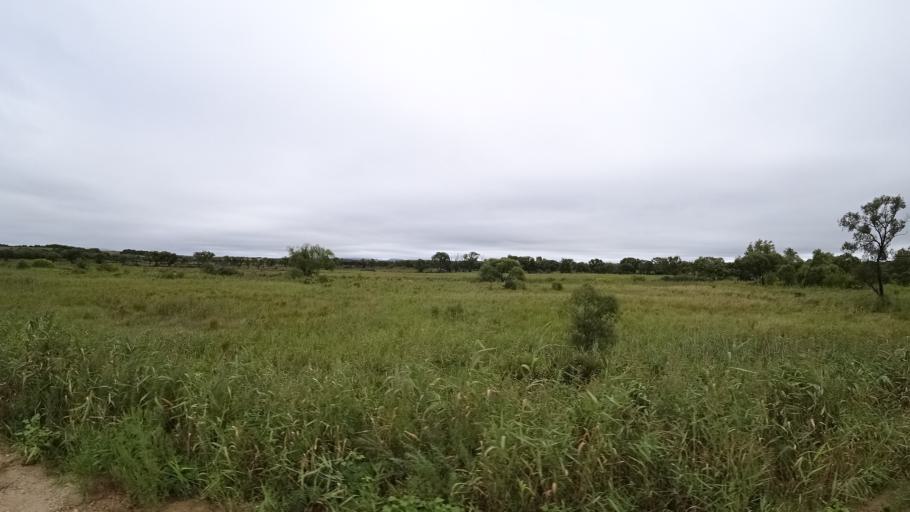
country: RU
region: Primorskiy
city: Ivanovka
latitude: 44.0711
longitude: 132.5807
